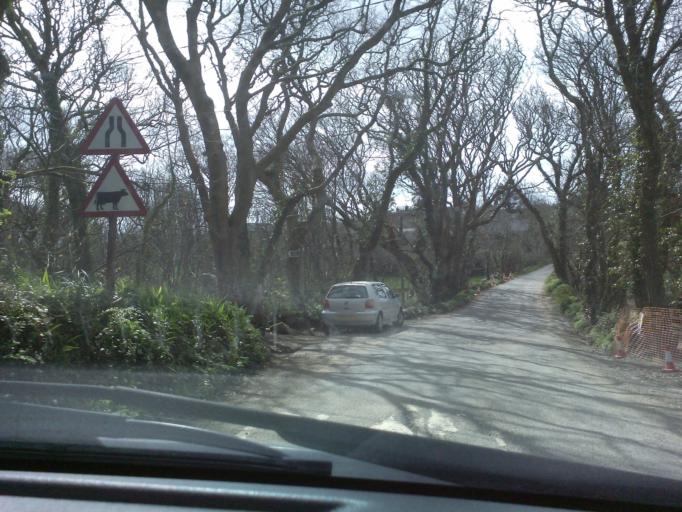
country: GB
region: England
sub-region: Cornwall
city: St. Buryan
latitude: 50.0590
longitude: -5.6078
